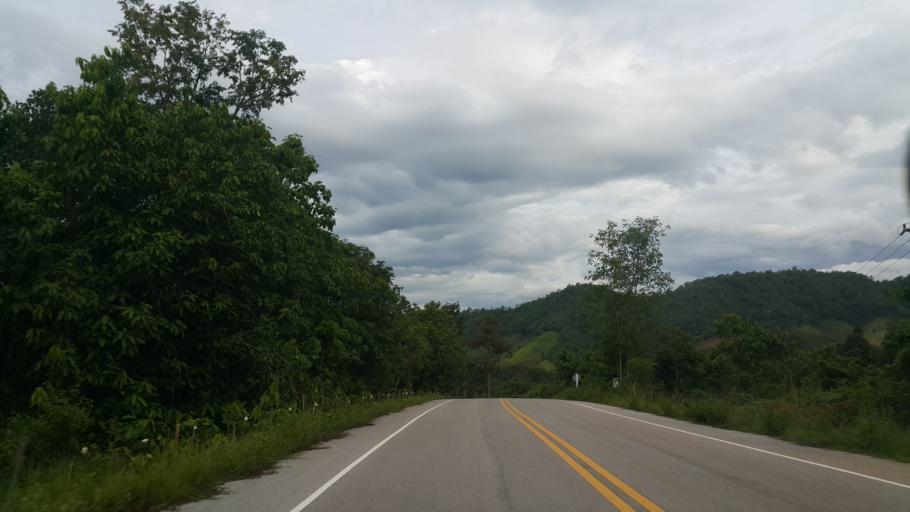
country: TH
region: Loei
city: Na Haeo
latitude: 17.5017
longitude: 101.0907
